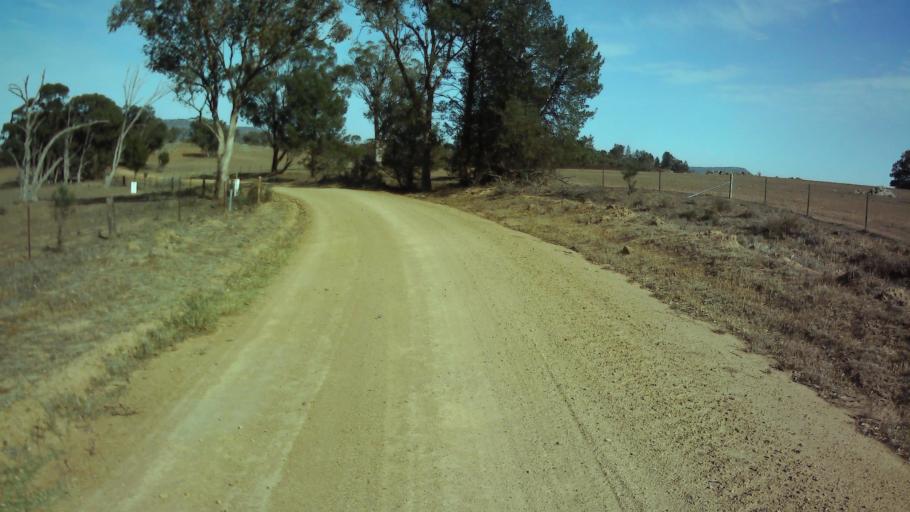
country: AU
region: New South Wales
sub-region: Weddin
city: Grenfell
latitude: -33.7545
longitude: 148.0235
